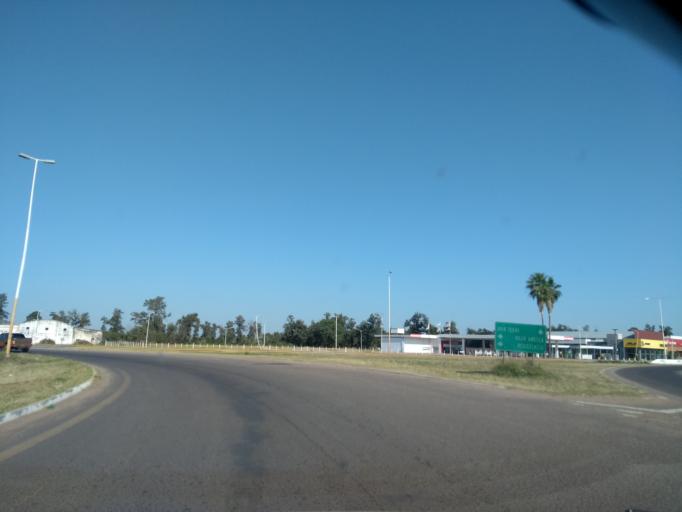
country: AR
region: Chaco
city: Presidencia Roque Saenz Pena
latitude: -26.8120
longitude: -60.4188
